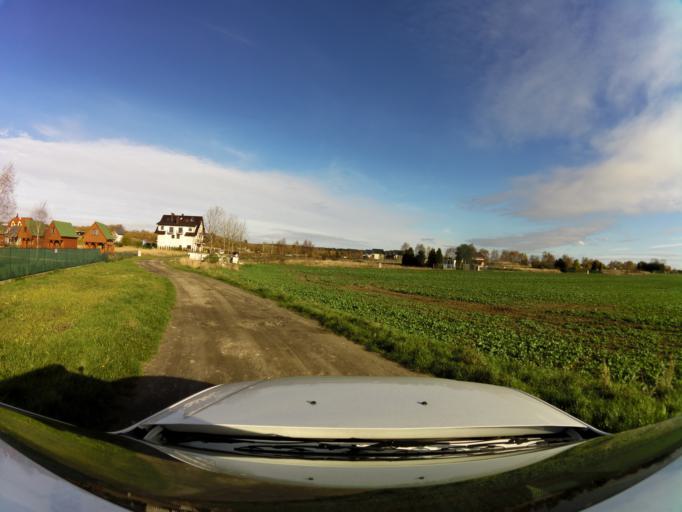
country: PL
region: West Pomeranian Voivodeship
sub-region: Powiat gryficki
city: Rewal
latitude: 54.0819
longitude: 15.0367
